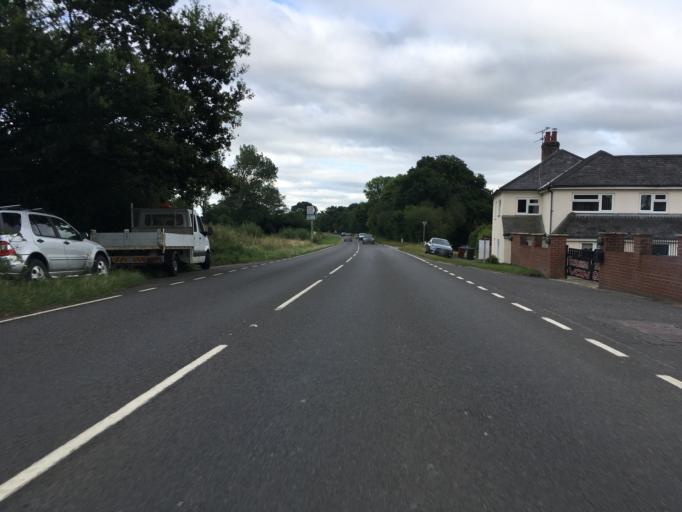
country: GB
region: England
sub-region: Hampshire
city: Liss
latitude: 51.0066
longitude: -0.8880
